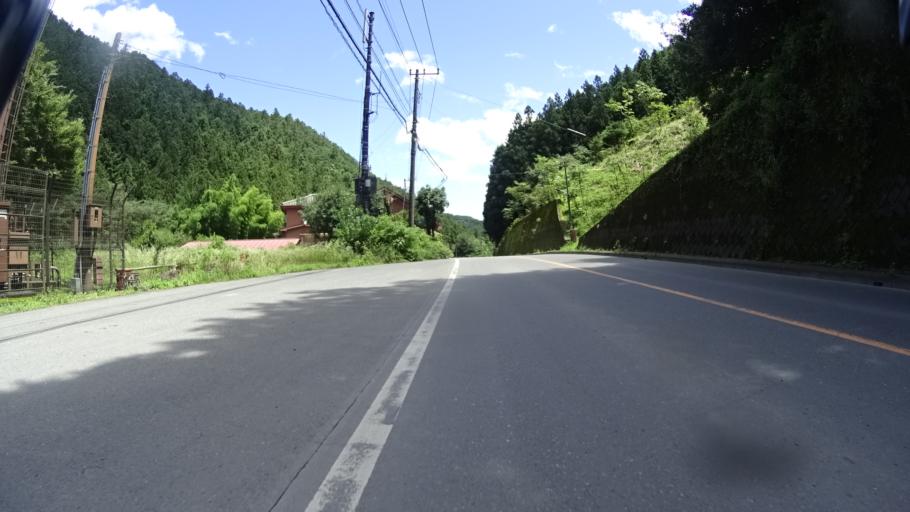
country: JP
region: Tokyo
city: Ome
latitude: 35.8201
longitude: 139.2334
